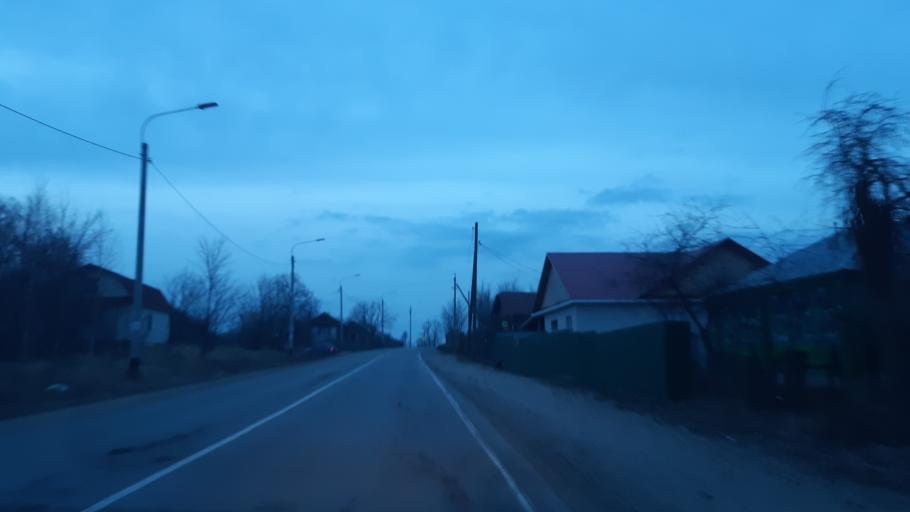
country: RU
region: Vladimir
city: Nikologory
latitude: 56.1595
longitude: 41.9958
